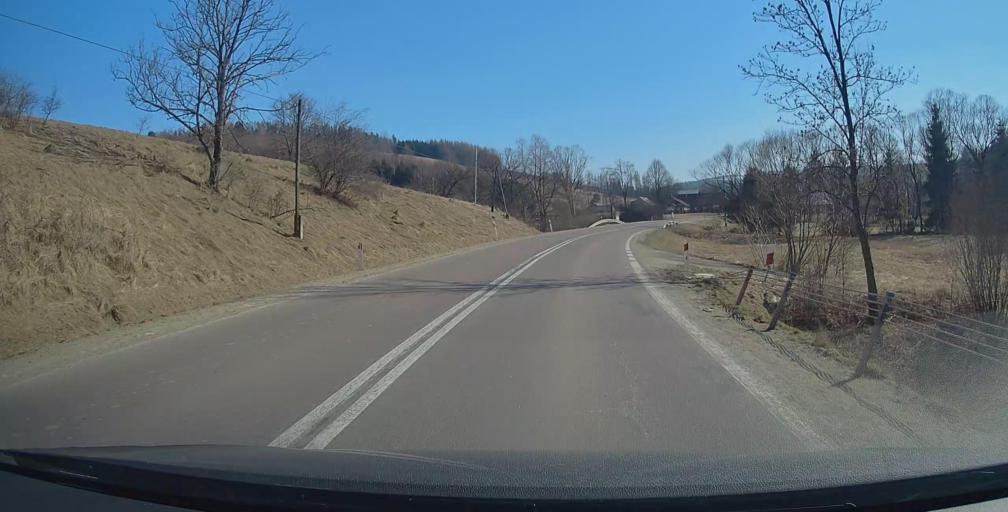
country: PL
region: Subcarpathian Voivodeship
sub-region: Powiat bieszczadzki
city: Ustrzyki Dolne
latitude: 49.5627
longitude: 22.5584
